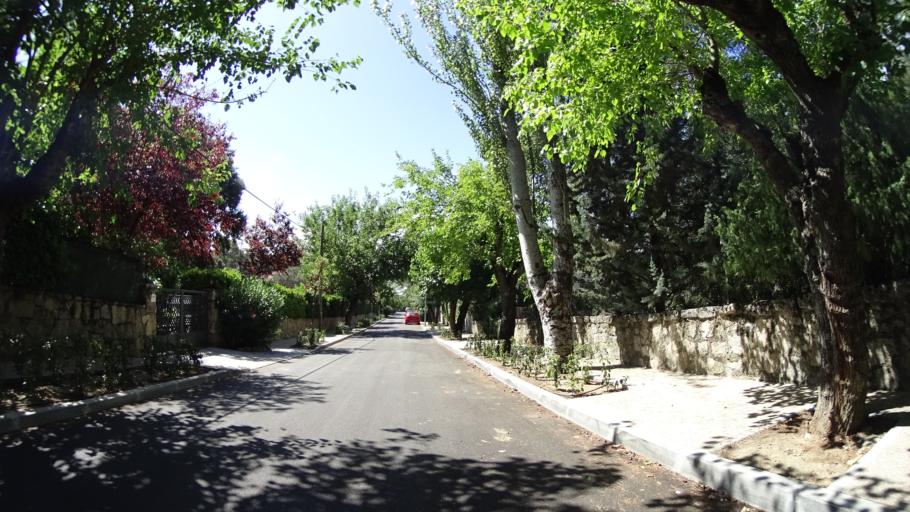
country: ES
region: Madrid
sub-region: Provincia de Madrid
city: Torrelodones
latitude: 40.5734
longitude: -3.9453
